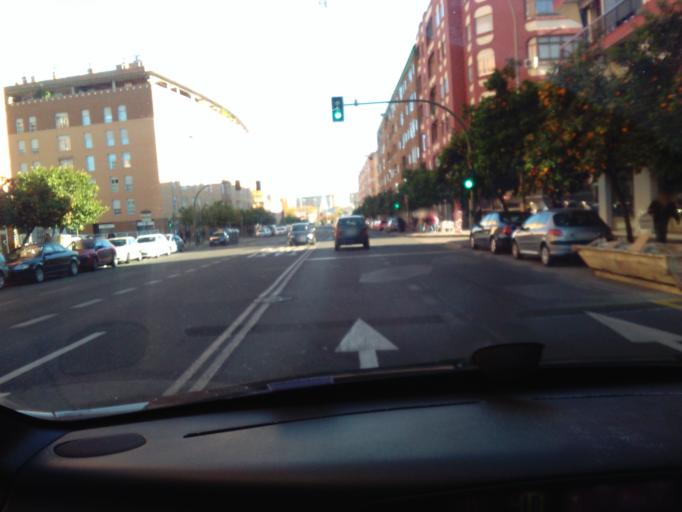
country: ES
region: Andalusia
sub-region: Provincia de Sevilla
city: Sevilla
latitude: 37.3930
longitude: -5.9810
